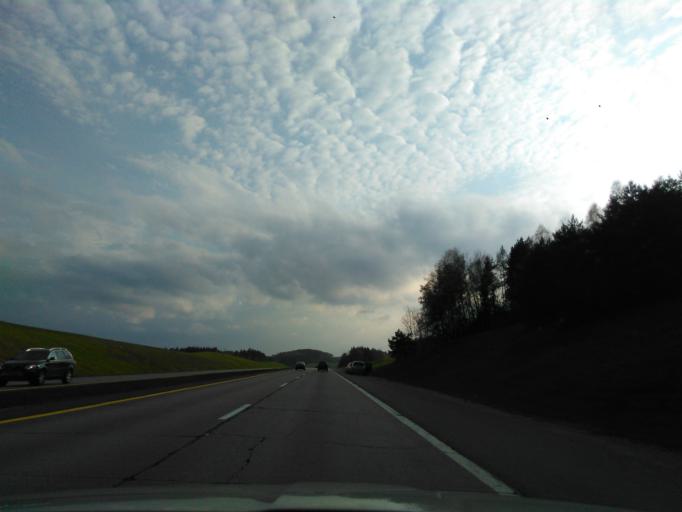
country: BY
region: Minsk
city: Astrashytski Haradok
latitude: 54.0721
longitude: 27.7280
